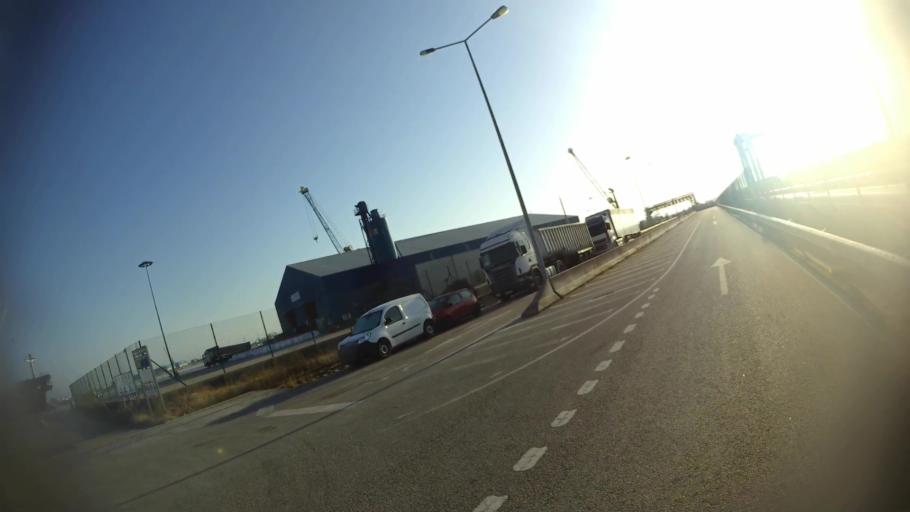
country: PT
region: Aveiro
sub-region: Ilhavo
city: Gafanha da Nazare
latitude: 40.6554
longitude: -8.7127
